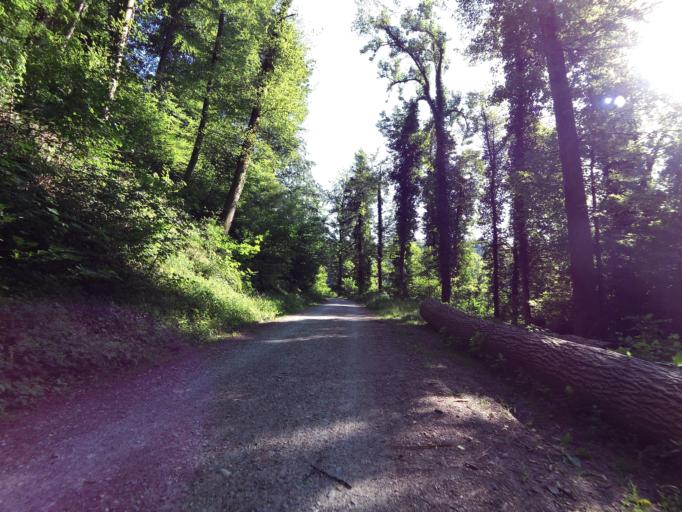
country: CH
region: Aargau
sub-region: Bezirk Lenzburg
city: Staufen
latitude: 47.3683
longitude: 8.1723
